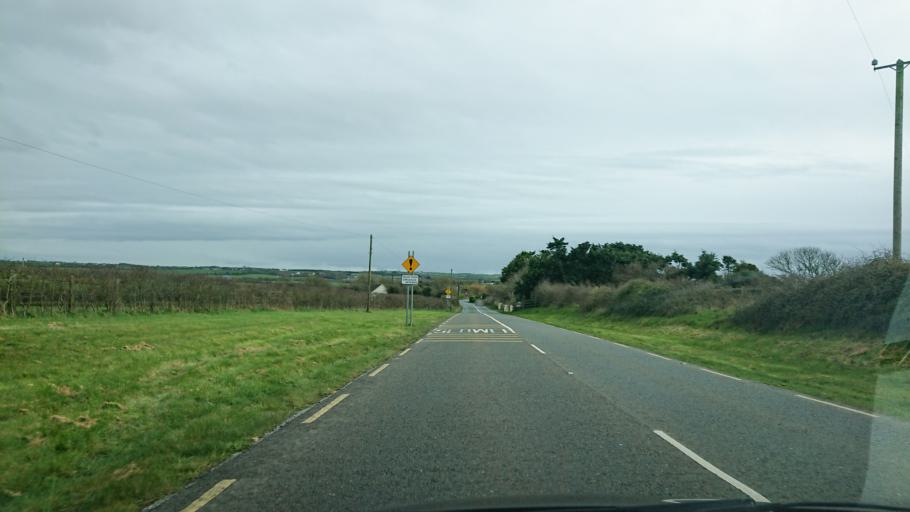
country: IE
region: Munster
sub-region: Waterford
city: Tra Mhor
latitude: 52.1820
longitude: -7.0753
